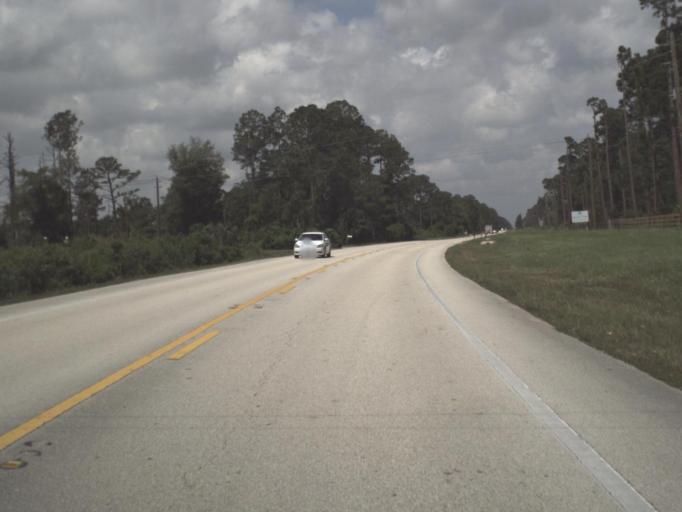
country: US
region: Florida
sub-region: Saint Johns County
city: Butler Beach
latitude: 29.7572
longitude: -81.2745
